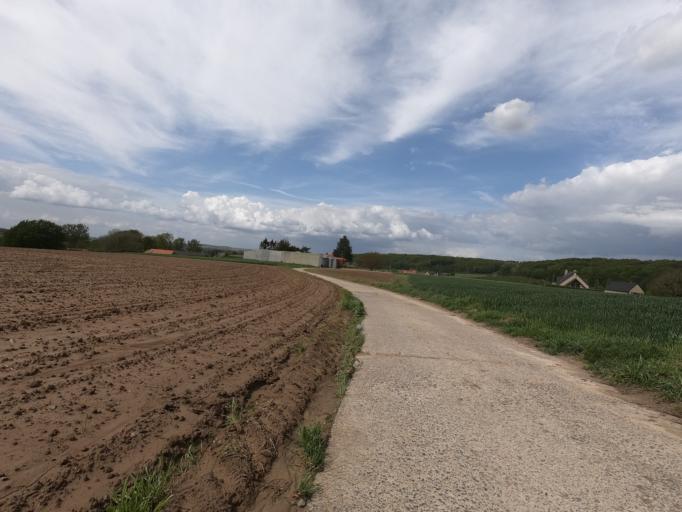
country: BE
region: Flanders
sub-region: Provincie Oost-Vlaanderen
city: Ronse
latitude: 50.7780
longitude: 3.5784
